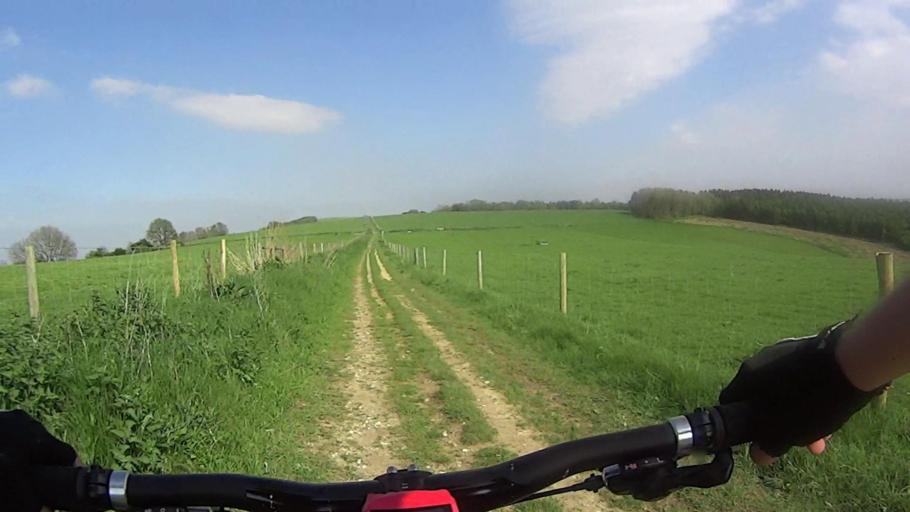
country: GB
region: England
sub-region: West Sussex
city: Midhurst
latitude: 50.9500
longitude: -0.8098
